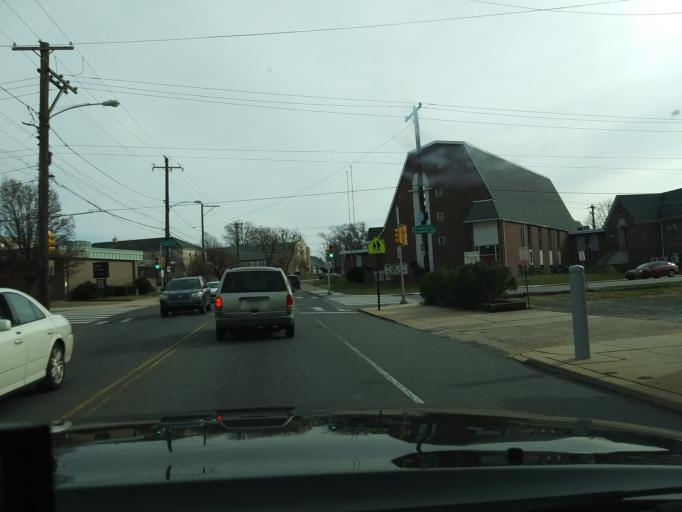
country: US
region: Pennsylvania
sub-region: Montgomery County
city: Rockledge
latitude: 40.0766
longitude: -75.0829
